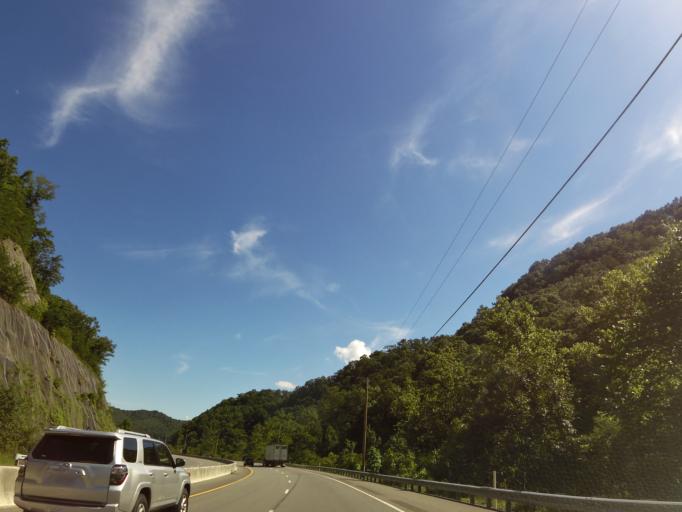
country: US
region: Tennessee
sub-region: Grainger County
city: Bean Station
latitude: 36.3527
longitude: -83.3392
